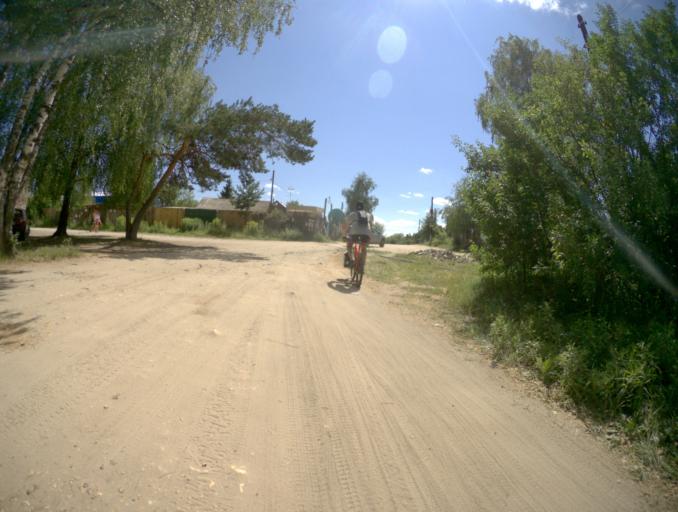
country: RU
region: Nizjnij Novgorod
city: Neklyudovo
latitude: 56.4533
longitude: 44.0064
